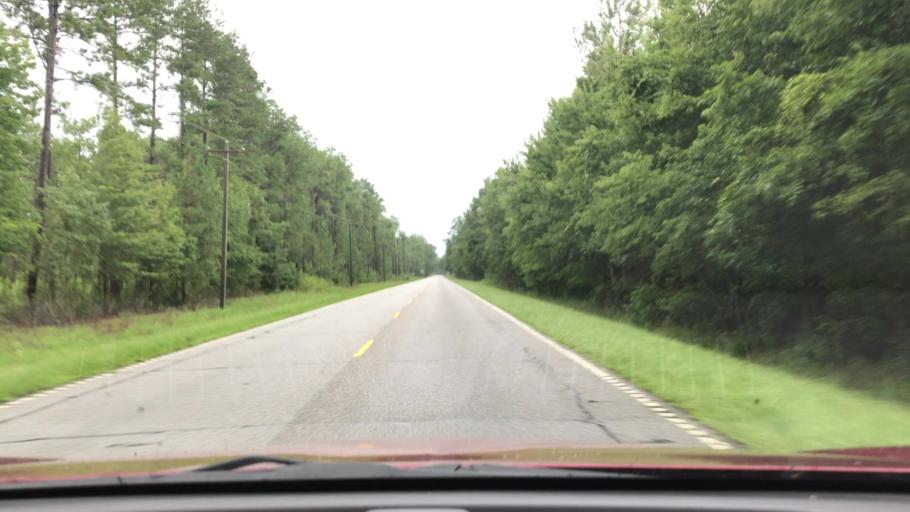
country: US
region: South Carolina
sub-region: Georgetown County
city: Murrells Inlet
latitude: 33.6058
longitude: -79.1988
